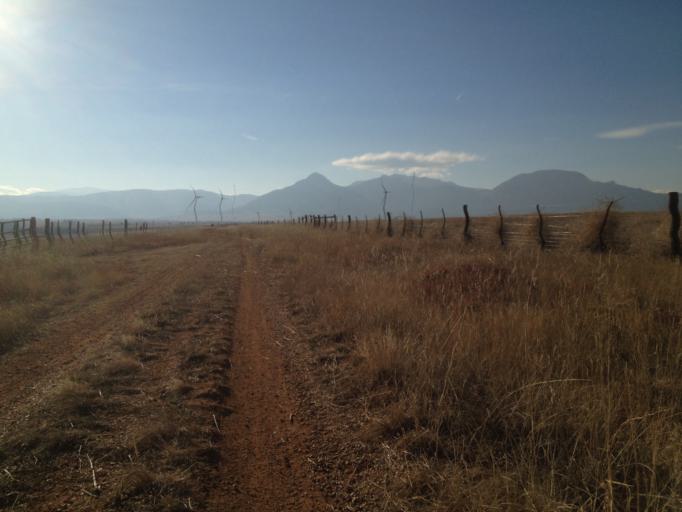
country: US
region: Colorado
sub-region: Boulder County
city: Superior
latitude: 39.9159
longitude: -105.2027
